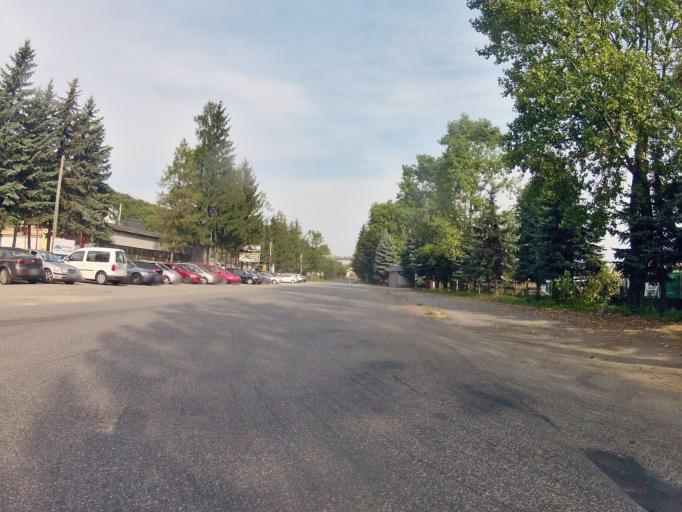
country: PL
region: Subcarpathian Voivodeship
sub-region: Powiat jasielski
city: Jaslo
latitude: 49.7197
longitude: 21.4531
